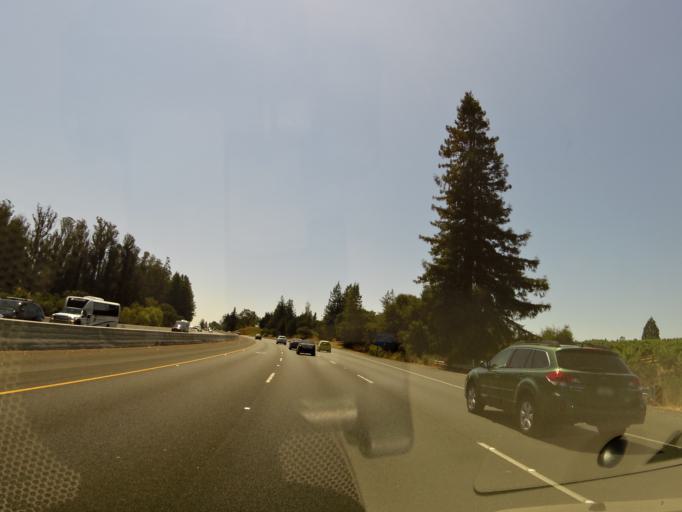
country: US
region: California
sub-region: Sonoma County
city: Cotati
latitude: 38.3120
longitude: -122.7148
